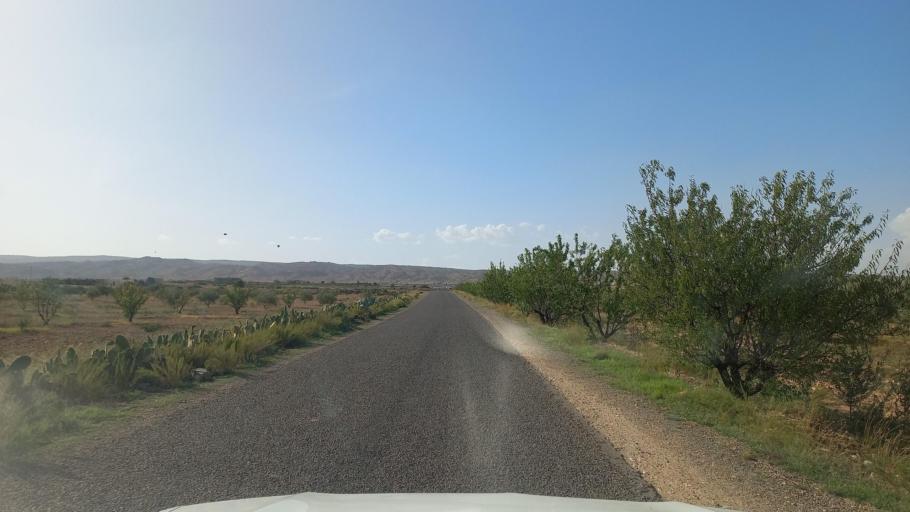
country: TN
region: Al Qasrayn
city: Sbiba
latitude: 35.3340
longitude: 9.0038
